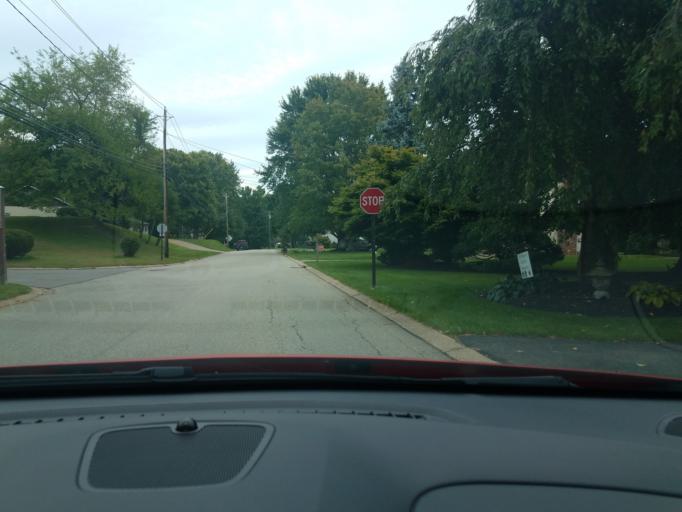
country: US
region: Pennsylvania
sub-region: Allegheny County
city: Franklin Park
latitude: 40.5667
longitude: -80.0717
